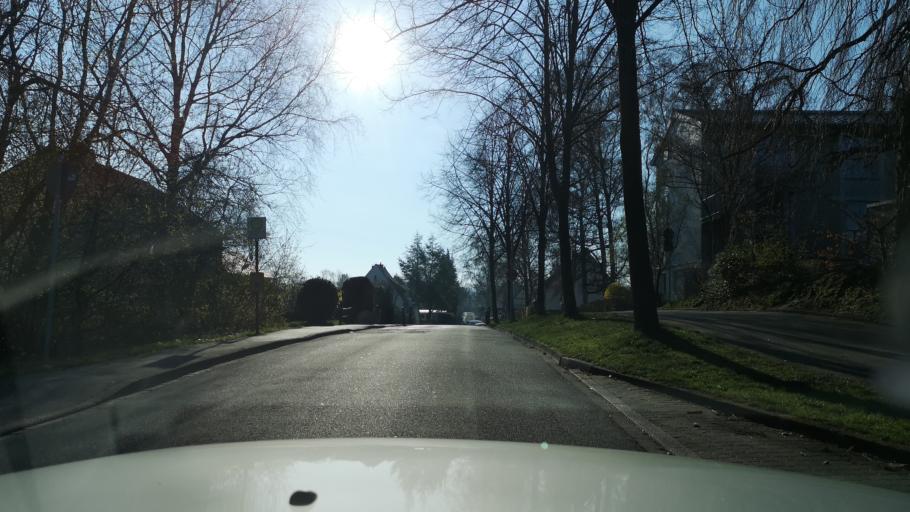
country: DE
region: North Rhine-Westphalia
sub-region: Regierungsbezirk Arnsberg
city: Menden
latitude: 51.4319
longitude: 7.7938
